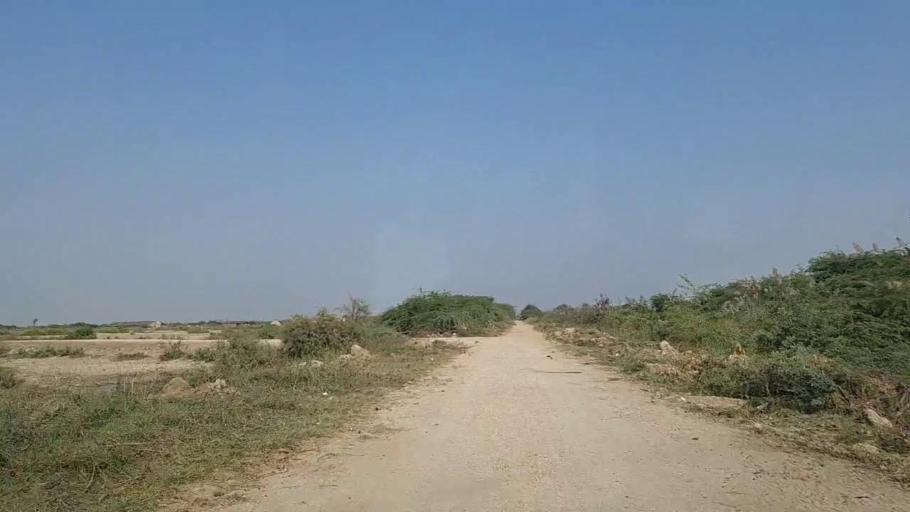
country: PK
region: Sindh
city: Mirpur Sakro
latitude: 24.6581
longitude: 67.7265
